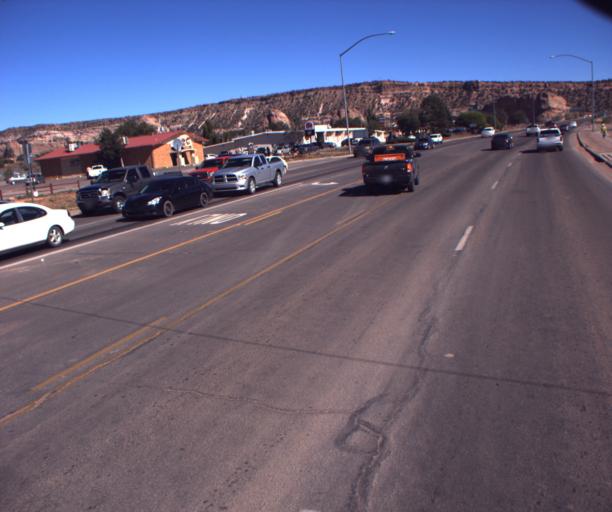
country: US
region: Arizona
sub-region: Apache County
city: Window Rock
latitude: 35.6633
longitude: -109.0568
